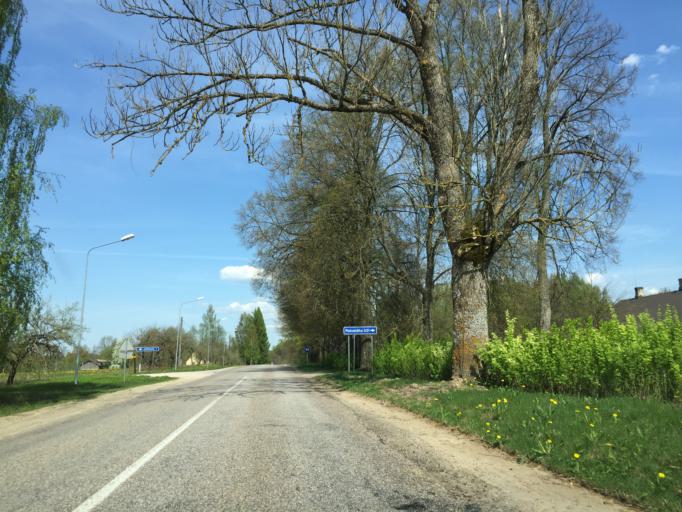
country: LV
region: Krimulda
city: Ragana
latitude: 57.3224
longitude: 24.6409
